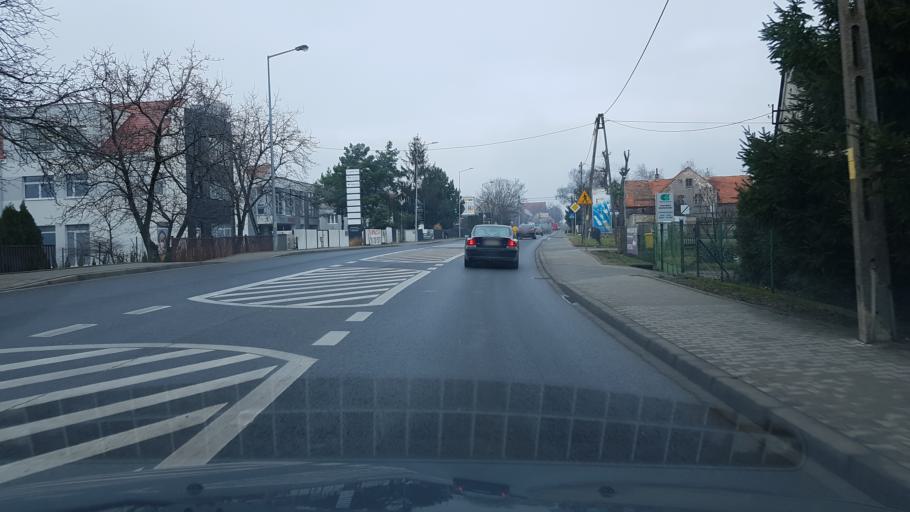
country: PL
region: Lower Silesian Voivodeship
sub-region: Powiat wroclawski
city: Bielany Wroclawskie
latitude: 51.0347
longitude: 16.9678
